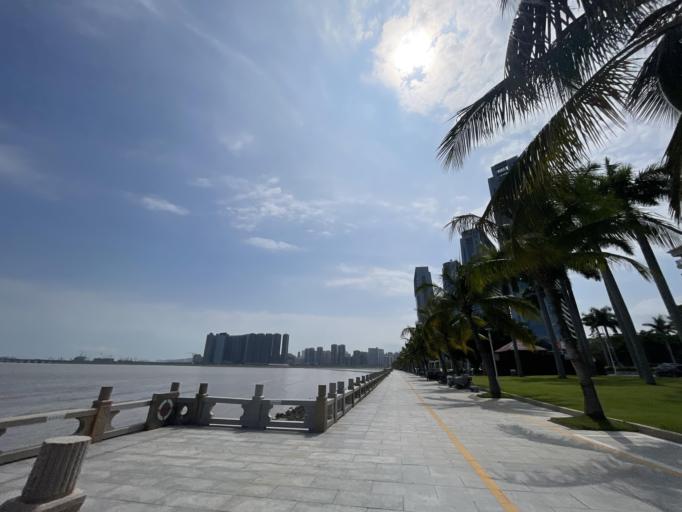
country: MO
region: Macau
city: Macau
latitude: 22.2266
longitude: 113.5572
